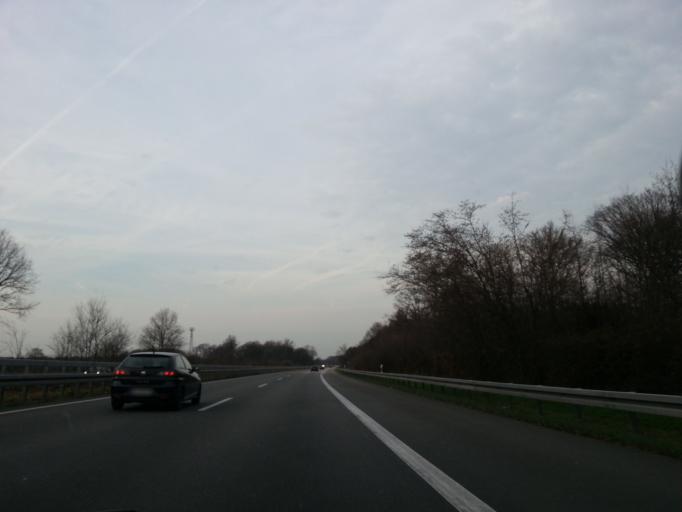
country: DE
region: North Rhine-Westphalia
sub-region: Regierungsbezirk Dusseldorf
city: Mehrhoog
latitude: 51.7872
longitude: 6.4997
